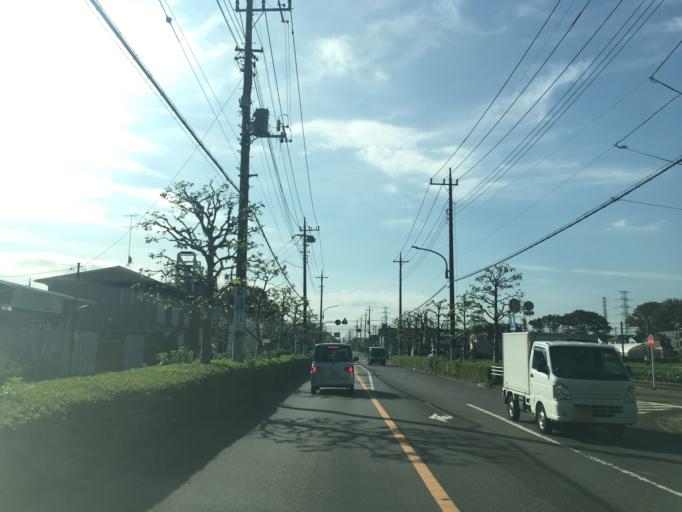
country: JP
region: Tokyo
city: Higashimurayama-shi
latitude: 35.7345
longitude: 139.4447
